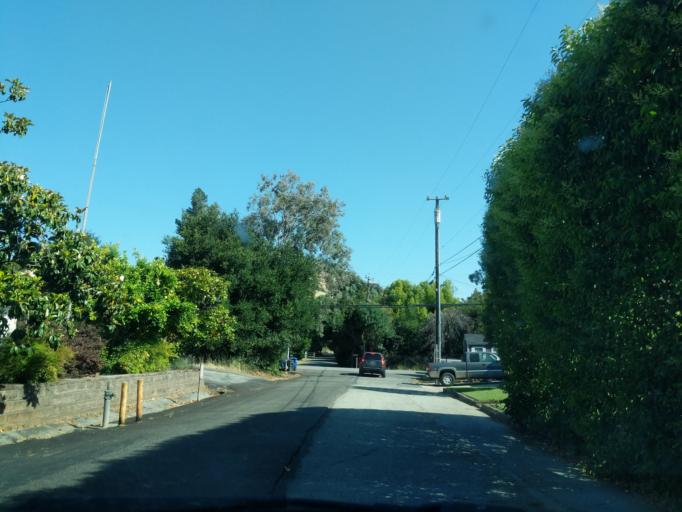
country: US
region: California
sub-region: Santa Clara County
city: Morgan Hill
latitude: 37.1041
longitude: -121.6627
